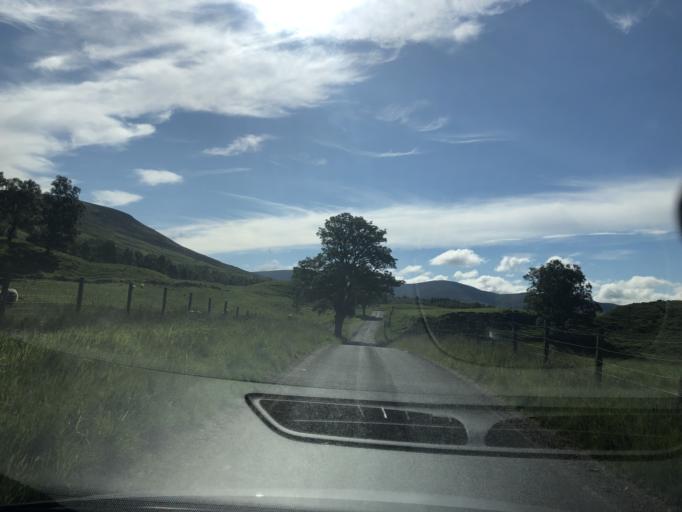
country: GB
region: Scotland
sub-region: Angus
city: Kirriemuir
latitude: 56.8425
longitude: -3.0976
